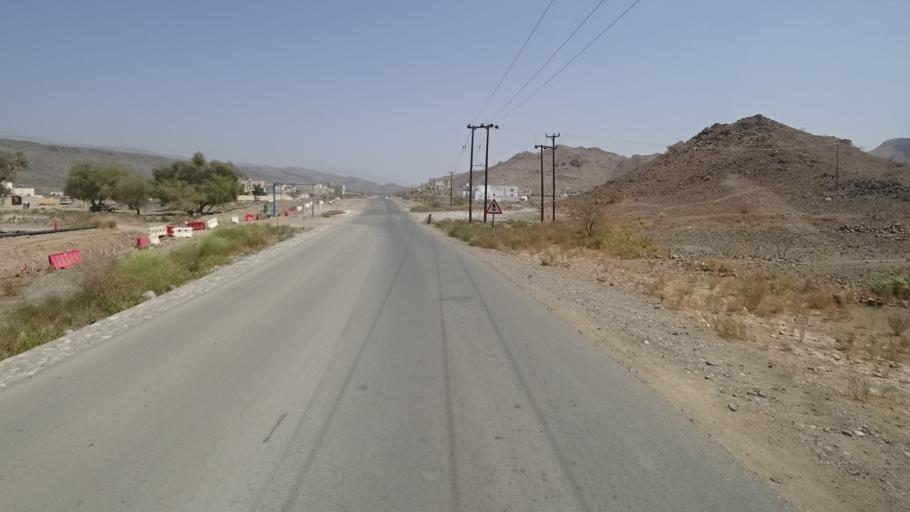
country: OM
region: Muhafazat ad Dakhiliyah
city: Bahla'
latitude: 23.0802
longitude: 57.3306
